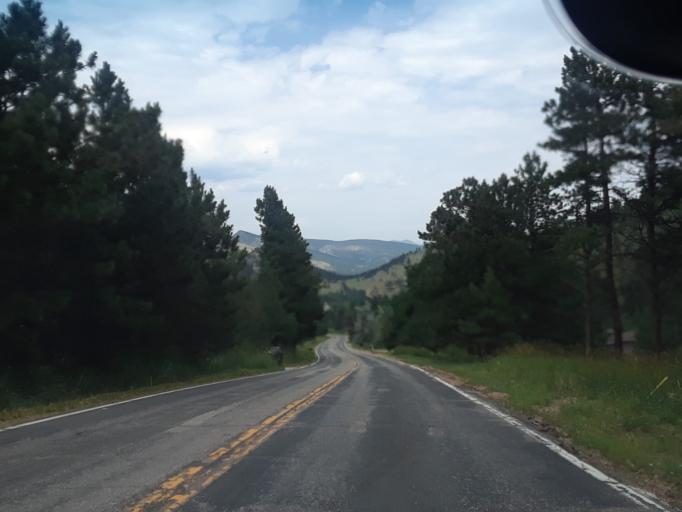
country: US
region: Colorado
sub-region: Boulder County
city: Boulder
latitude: 40.0936
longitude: -105.3019
